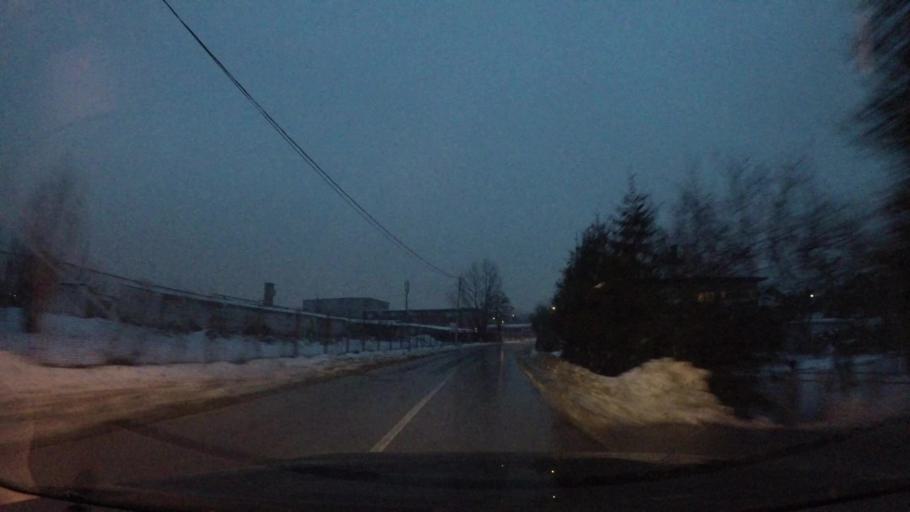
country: BA
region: Federation of Bosnia and Herzegovina
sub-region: Kanton Sarajevo
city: Sarajevo
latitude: 43.8465
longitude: 18.3201
